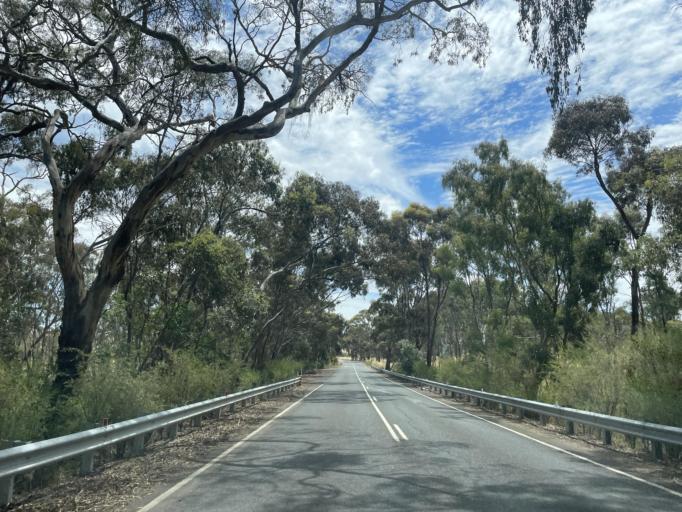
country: AU
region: South Australia
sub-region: Clare and Gilbert Valleys
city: Clare
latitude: -33.8992
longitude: 138.6879
